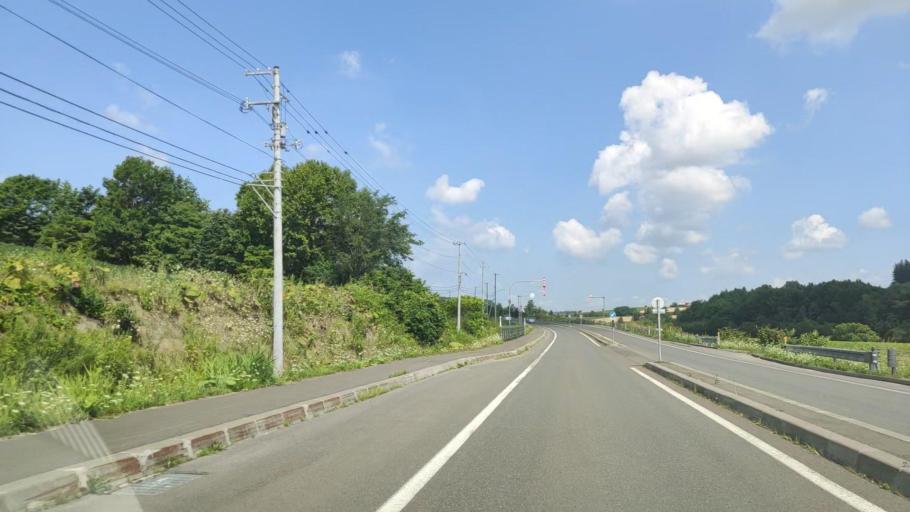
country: JP
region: Hokkaido
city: Shimo-furano
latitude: 43.5290
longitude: 142.4448
